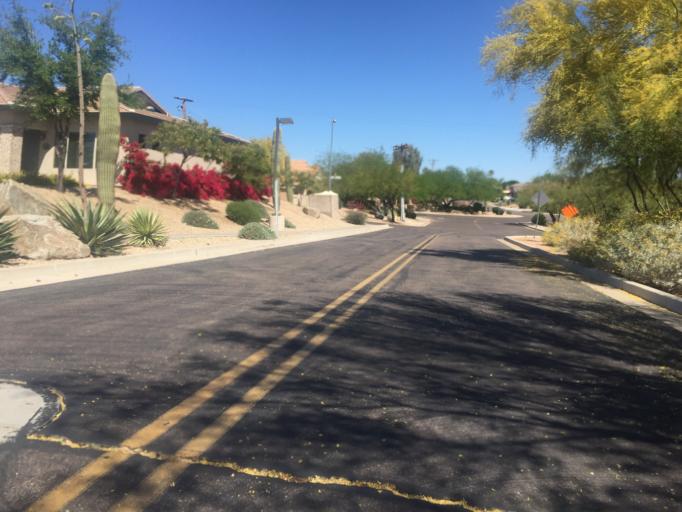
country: US
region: Arizona
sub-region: Maricopa County
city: Paradise Valley
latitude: 33.5716
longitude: -112.0262
